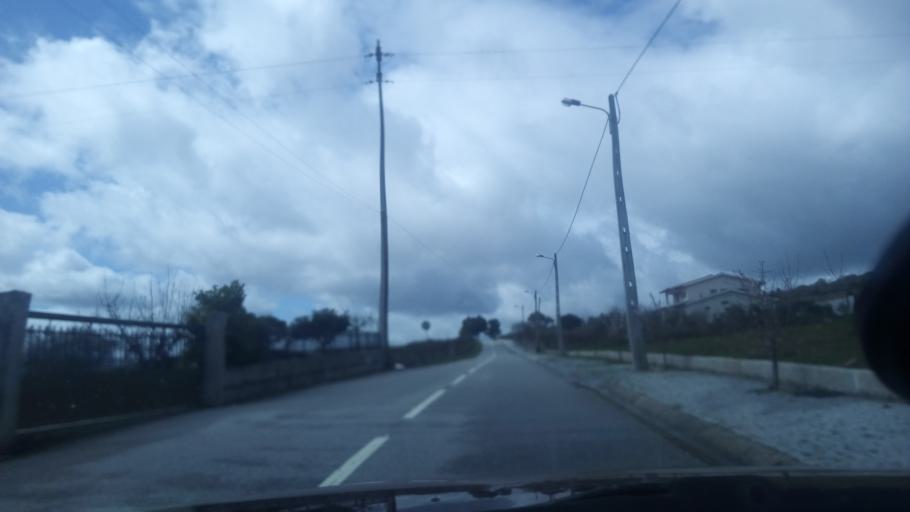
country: PT
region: Guarda
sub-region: Fornos de Algodres
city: Fornos de Algodres
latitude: 40.6067
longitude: -7.4935
